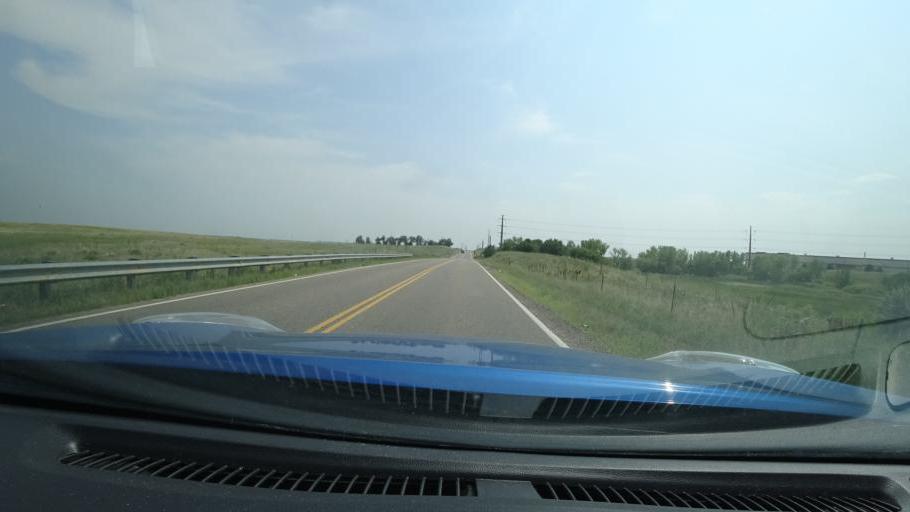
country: US
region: Colorado
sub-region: Adams County
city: Aurora
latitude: 39.7685
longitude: -104.7346
